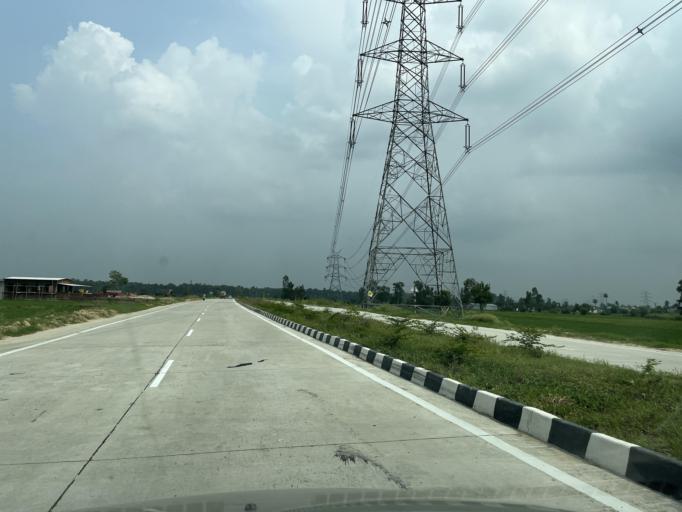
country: IN
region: Uttarakhand
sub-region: Udham Singh Nagar
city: Jaspur
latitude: 29.2824
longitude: 78.8613
